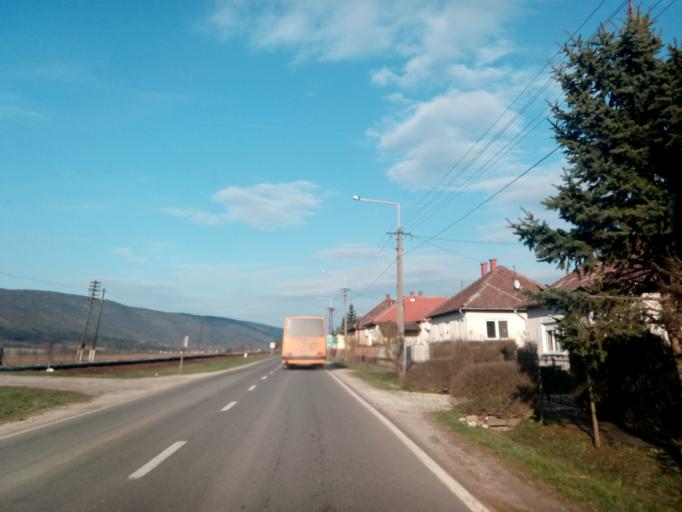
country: HU
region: Borsod-Abauj-Zemplen
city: Szendro
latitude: 48.5459
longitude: 20.7561
